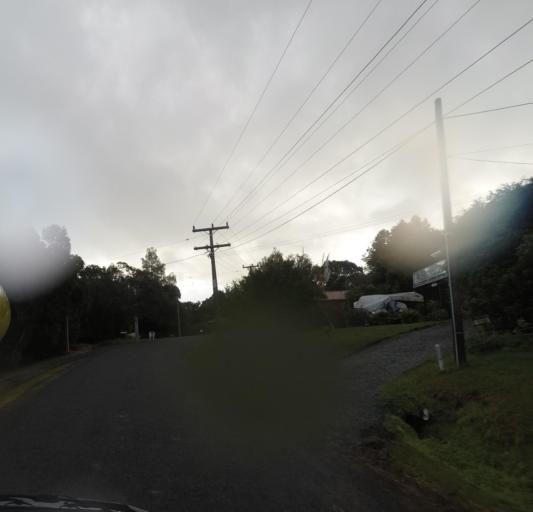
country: NZ
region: Auckland
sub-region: Auckland
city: Warkworth
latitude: -36.3820
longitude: 174.7625
